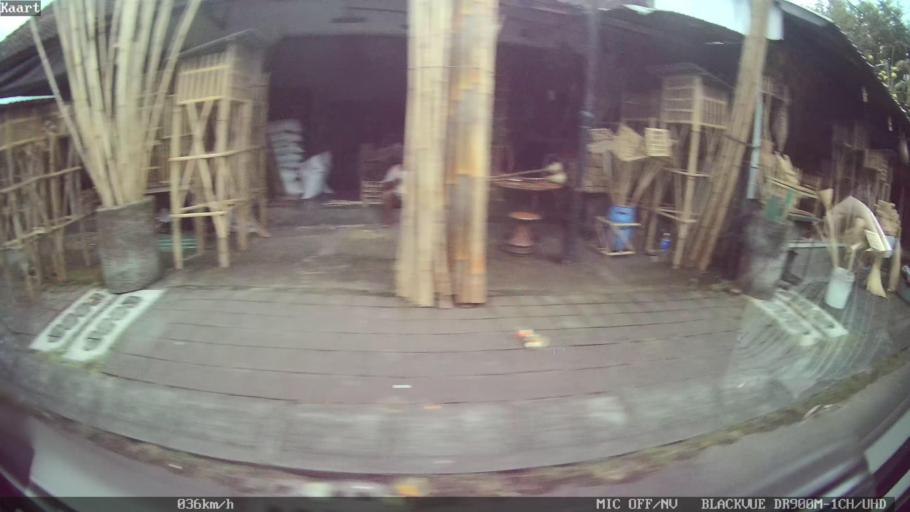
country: ID
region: Bali
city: Banjar Pekenjelodan
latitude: -8.5670
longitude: 115.1824
